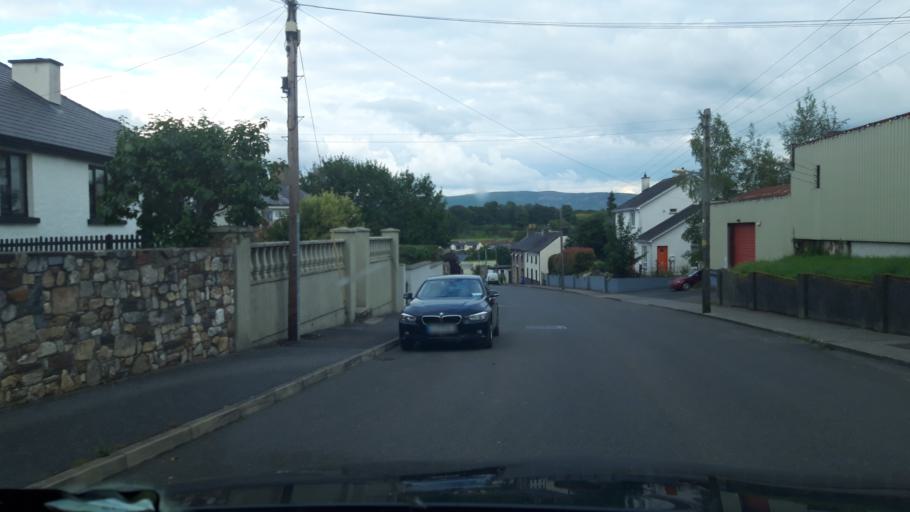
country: IE
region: Leinster
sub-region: Kilkenny
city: Graiguenamanagh
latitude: 52.5406
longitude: -6.9590
